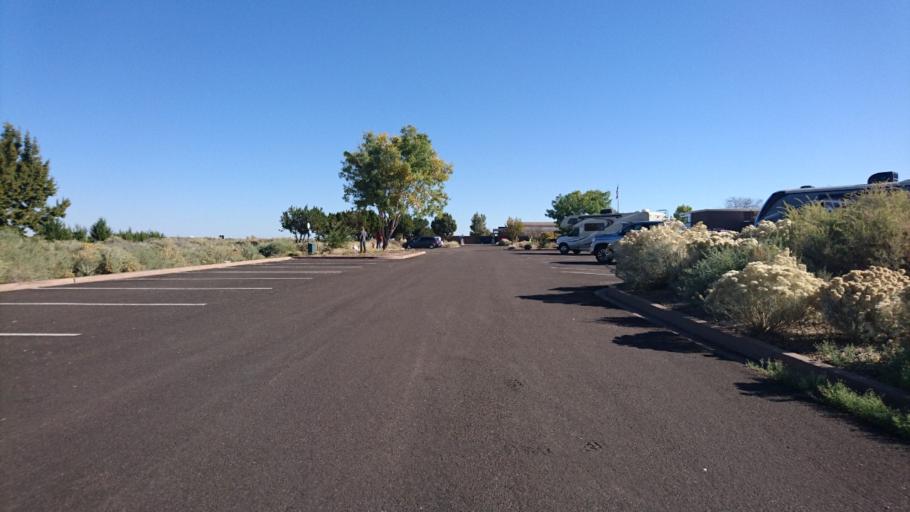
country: US
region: Arizona
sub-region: Navajo County
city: Holbrook
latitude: 35.0652
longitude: -109.7832
